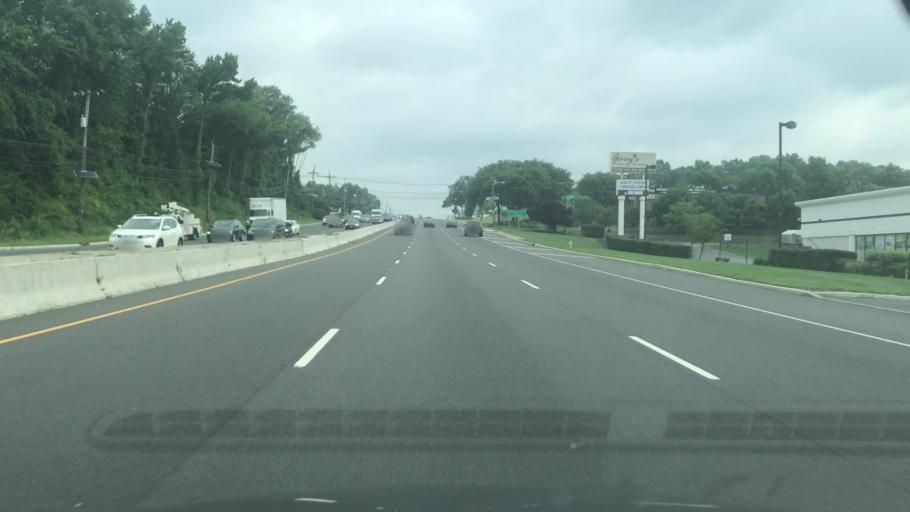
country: US
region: New Jersey
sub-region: Passaic County
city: Wayne
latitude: 40.9284
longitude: -74.2685
